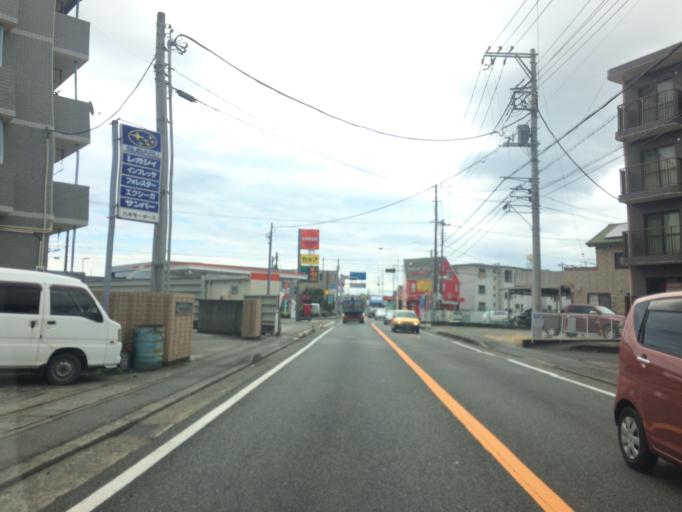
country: JP
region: Shizuoka
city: Fuji
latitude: 35.1464
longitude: 138.6467
